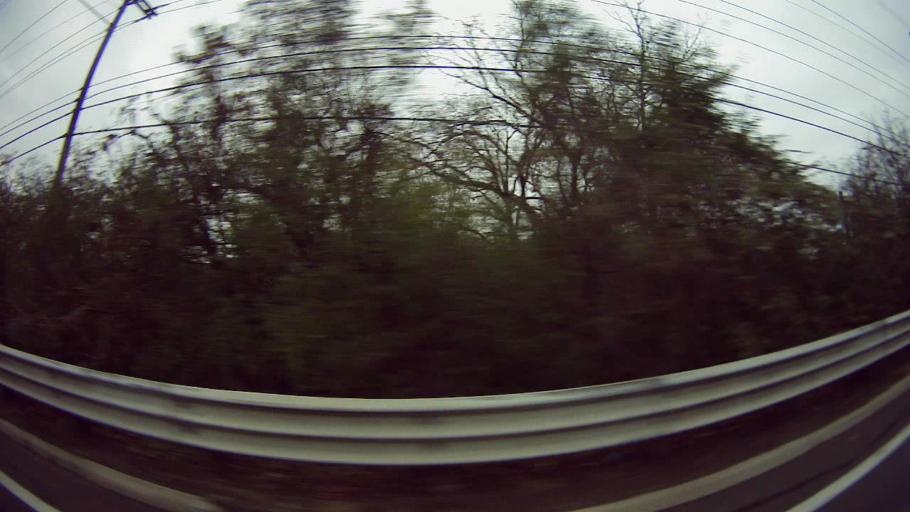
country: US
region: Michigan
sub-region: Wayne County
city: Dearborn Heights
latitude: 42.3491
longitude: -83.2741
